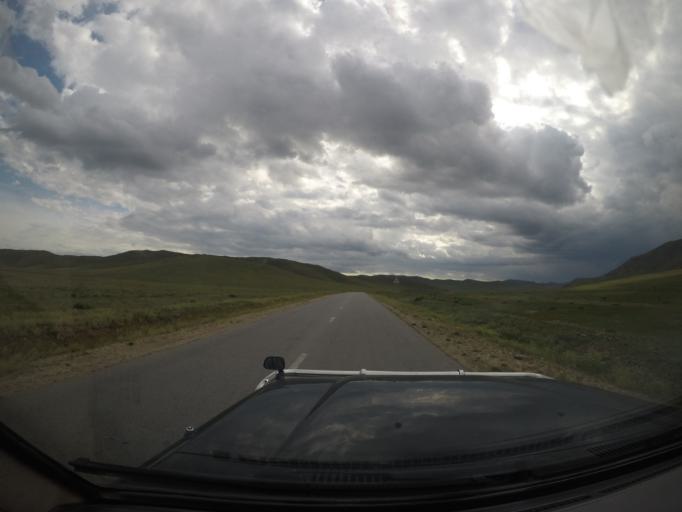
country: MN
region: Central Aimak
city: Bayandelger
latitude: 47.7001
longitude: 108.5557
